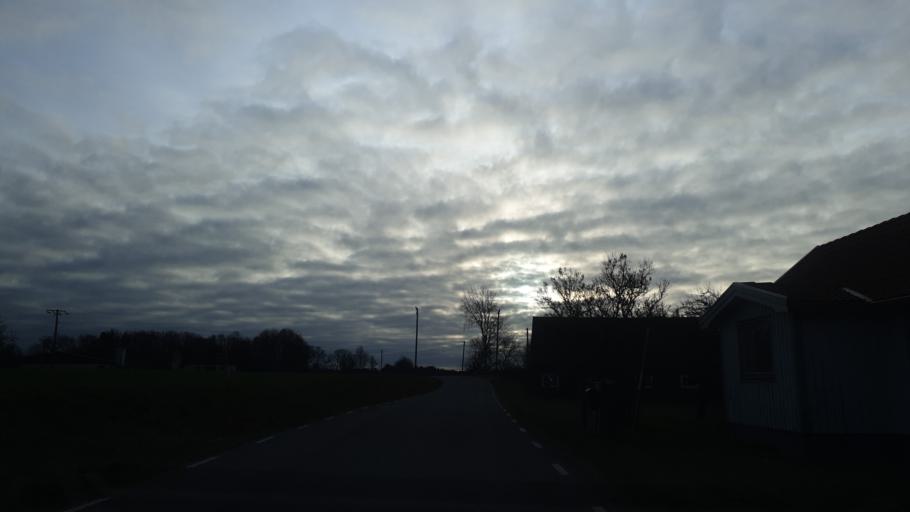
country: SE
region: Kalmar
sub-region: Torsas Kommun
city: Torsas
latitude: 56.3209
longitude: 16.0388
